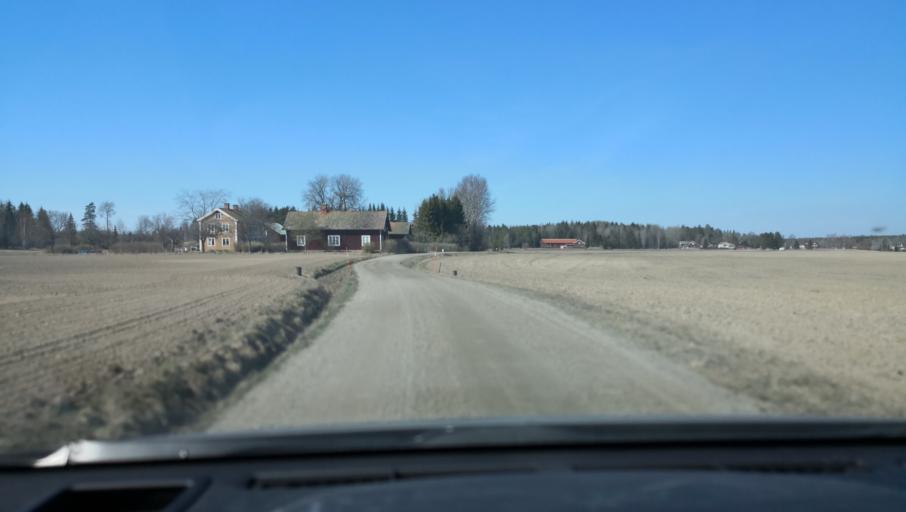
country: SE
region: Vaestmanland
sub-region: Sala Kommun
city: Sala
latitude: 59.8986
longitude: 16.5293
